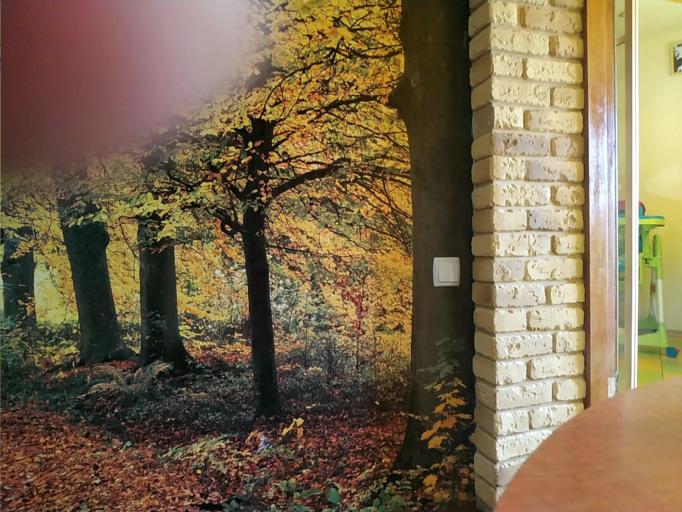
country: RU
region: Vologda
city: Nelazskoye
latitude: 59.4695
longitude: 37.6057
